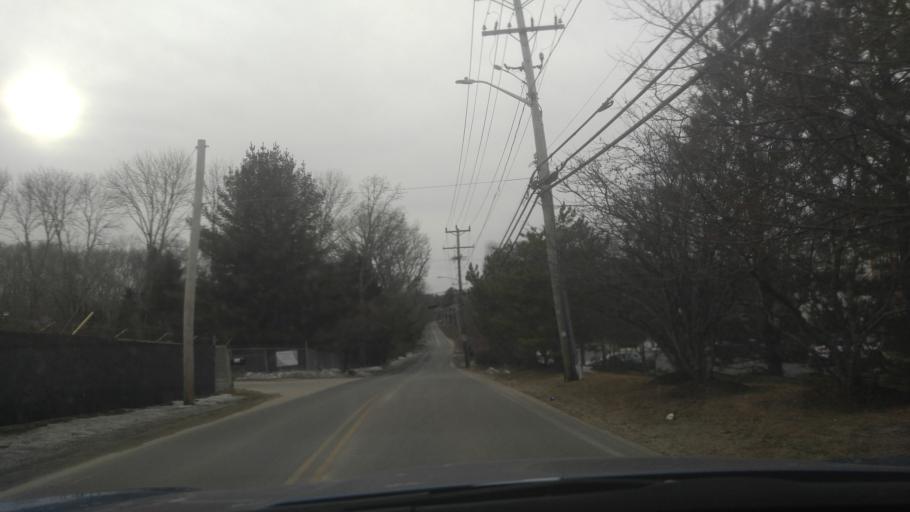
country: US
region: Rhode Island
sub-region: Kent County
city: West Warwick
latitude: 41.6737
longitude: -71.5028
